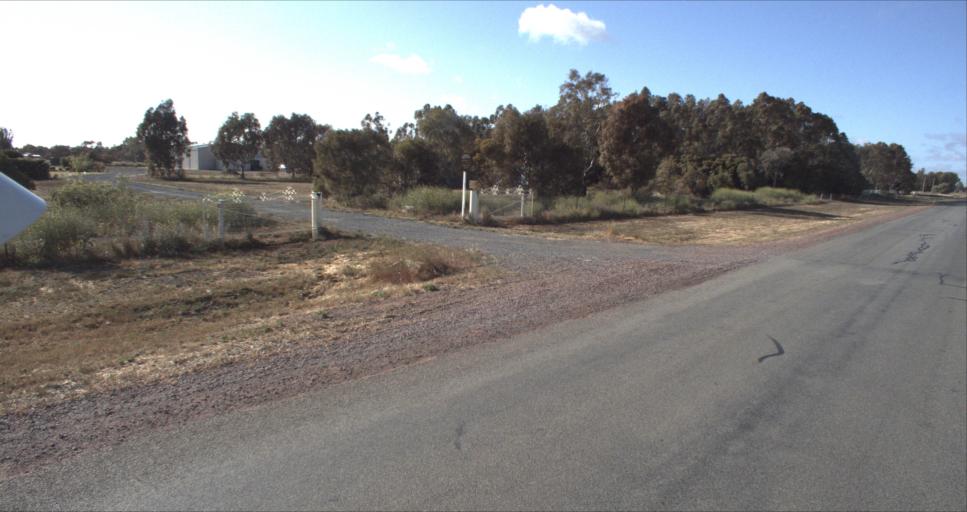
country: AU
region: New South Wales
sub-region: Leeton
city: Leeton
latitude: -34.5277
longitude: 146.3893
